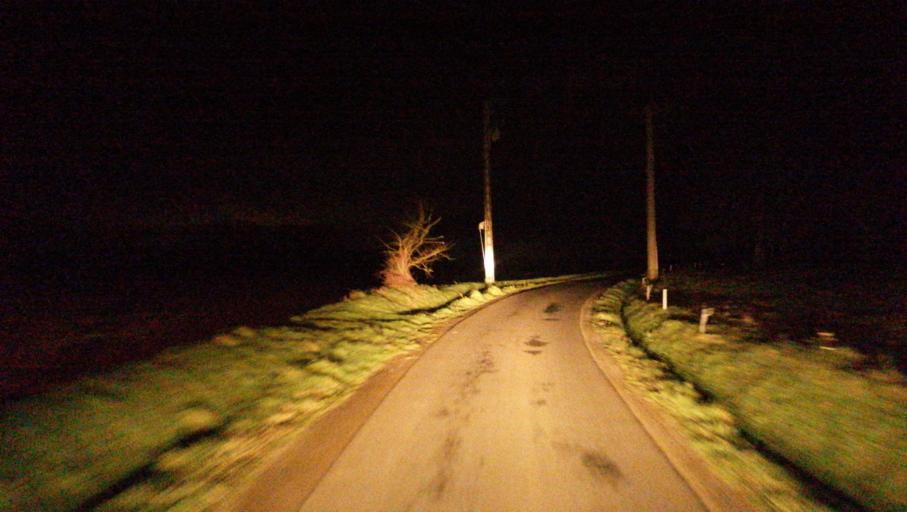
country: FR
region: Brittany
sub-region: Departement des Cotes-d'Armor
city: Saint-Agathon
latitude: 48.5742
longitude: -3.0774
